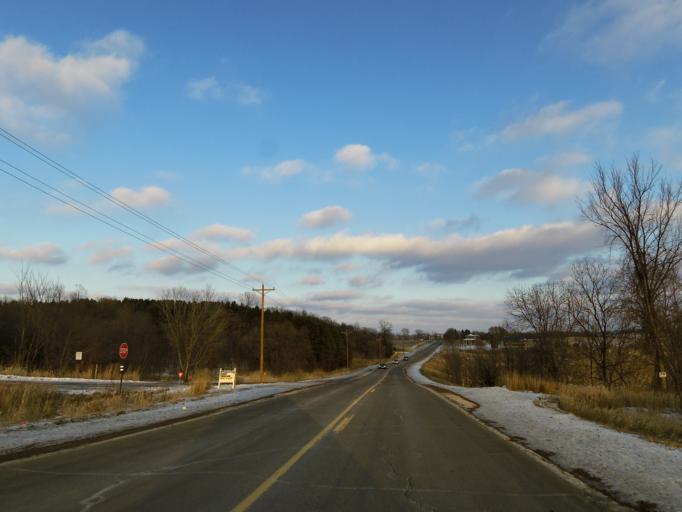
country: US
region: Minnesota
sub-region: Scott County
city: Prior Lake
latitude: 44.6303
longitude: -93.4275
